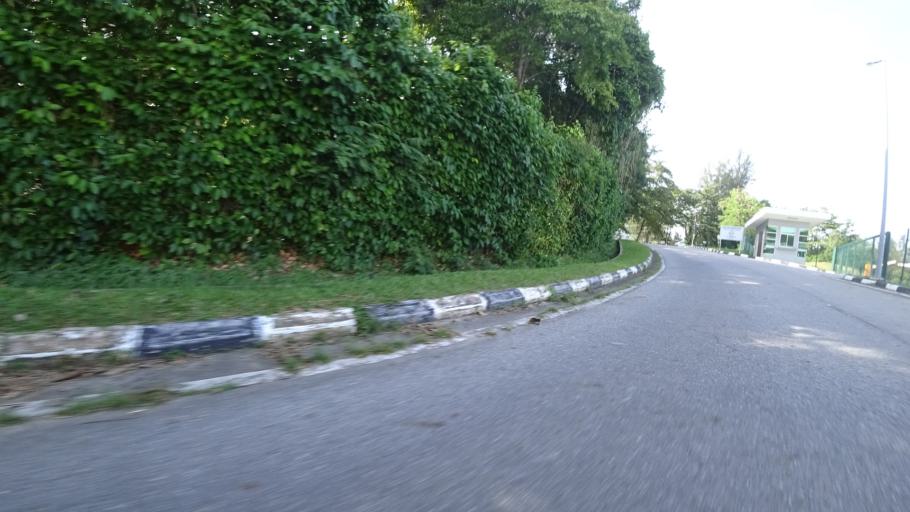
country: BN
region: Brunei and Muara
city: Bandar Seri Begawan
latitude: 4.9494
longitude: 114.8336
